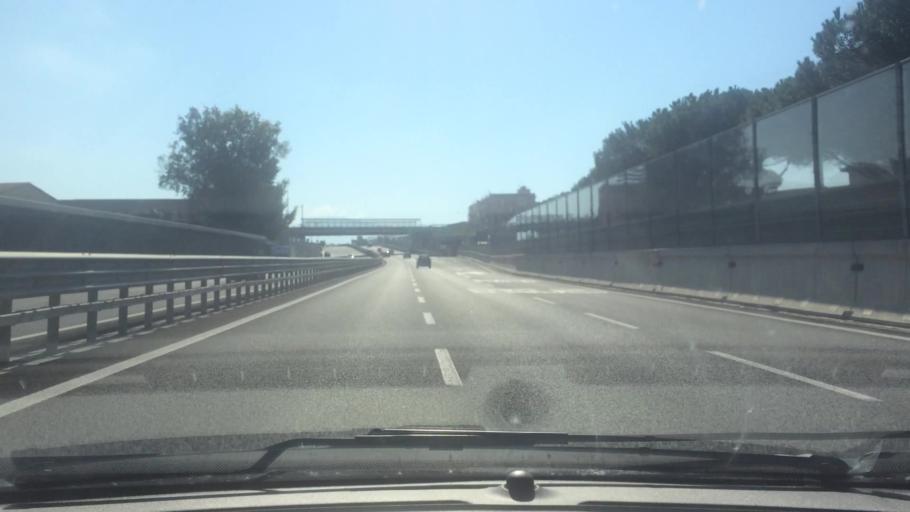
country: IT
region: Campania
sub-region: Provincia di Napoli
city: Ercolano
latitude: 40.8187
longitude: 14.3533
